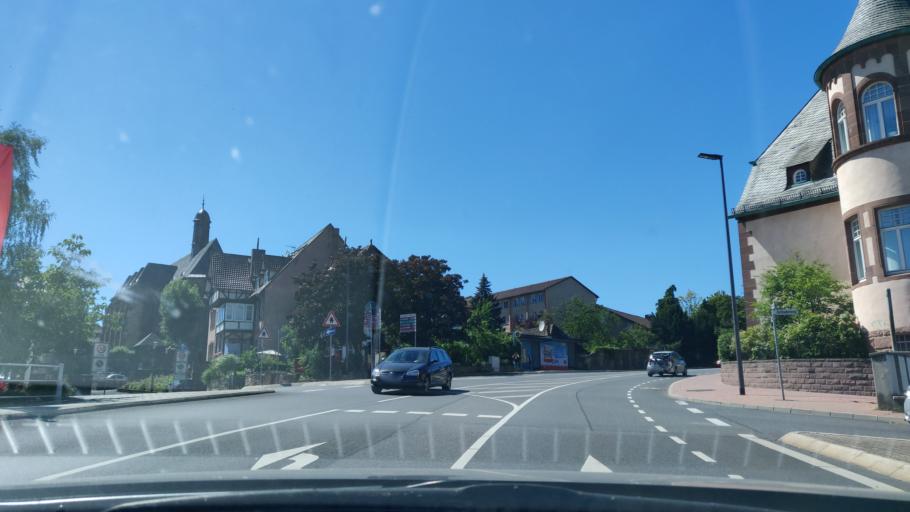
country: DE
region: Hesse
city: Fritzlar
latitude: 51.1323
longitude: 9.2796
